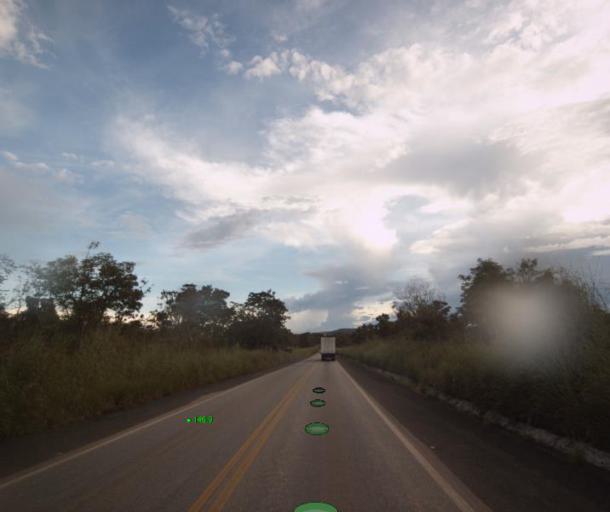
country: BR
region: Goias
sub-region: Uruacu
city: Uruacu
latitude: -14.0591
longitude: -49.0914
